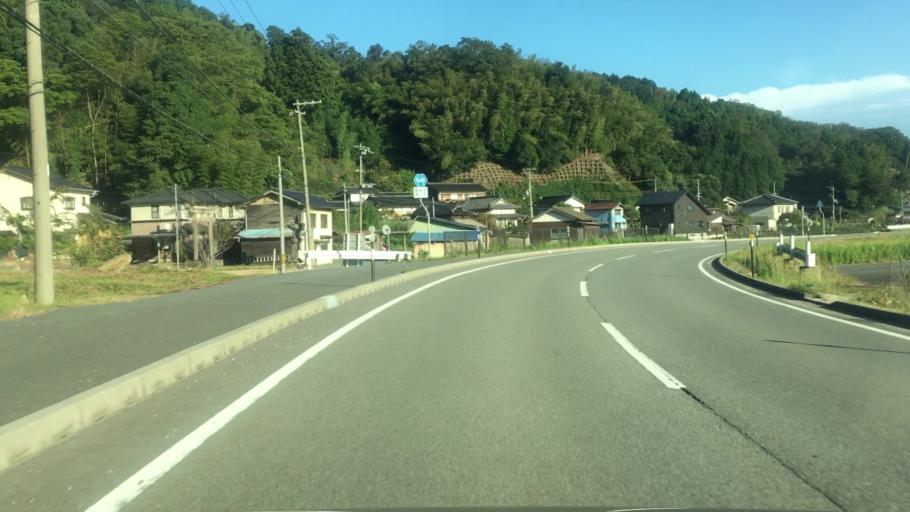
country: JP
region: Hyogo
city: Toyooka
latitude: 35.5852
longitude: 134.8085
